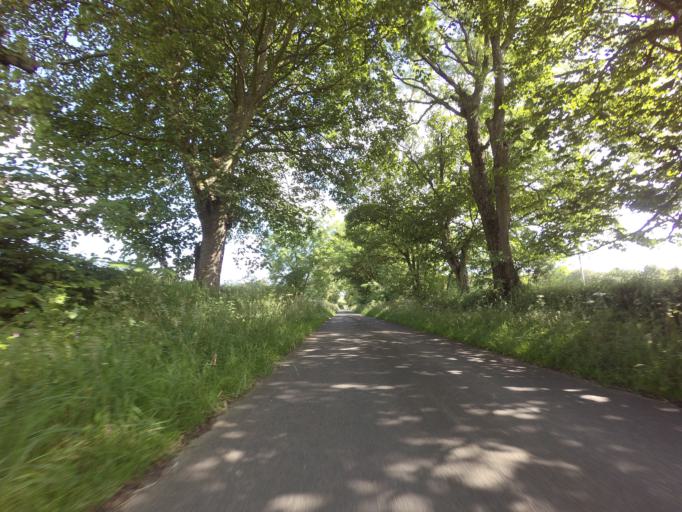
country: GB
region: Scotland
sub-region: Aberdeenshire
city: Turriff
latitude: 57.5903
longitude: -2.5053
